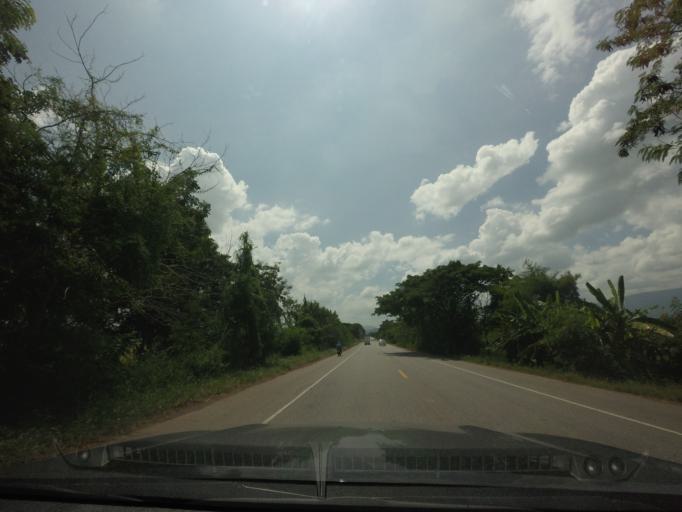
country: TH
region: Phetchabun
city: Phetchabun
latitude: 16.4525
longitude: 101.1149
